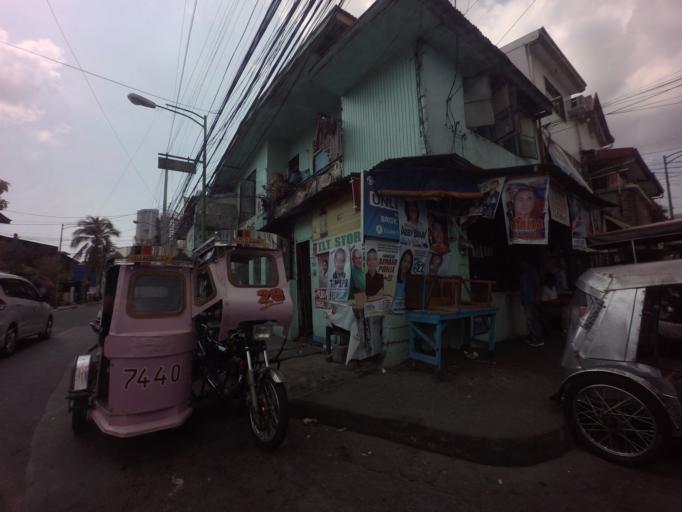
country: PH
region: Metro Manila
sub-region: Mandaluyong
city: Mandaluyong City
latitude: 14.5720
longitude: 121.0214
